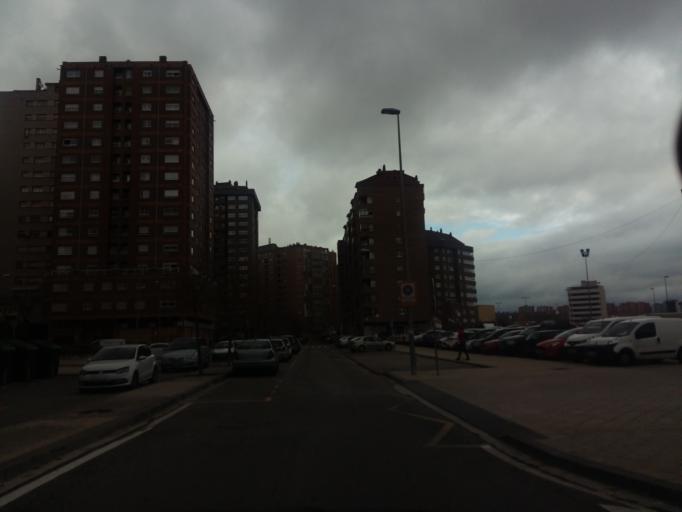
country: ES
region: Navarre
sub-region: Provincia de Navarra
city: Segundo Ensanche
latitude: 42.7997
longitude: -1.6457
